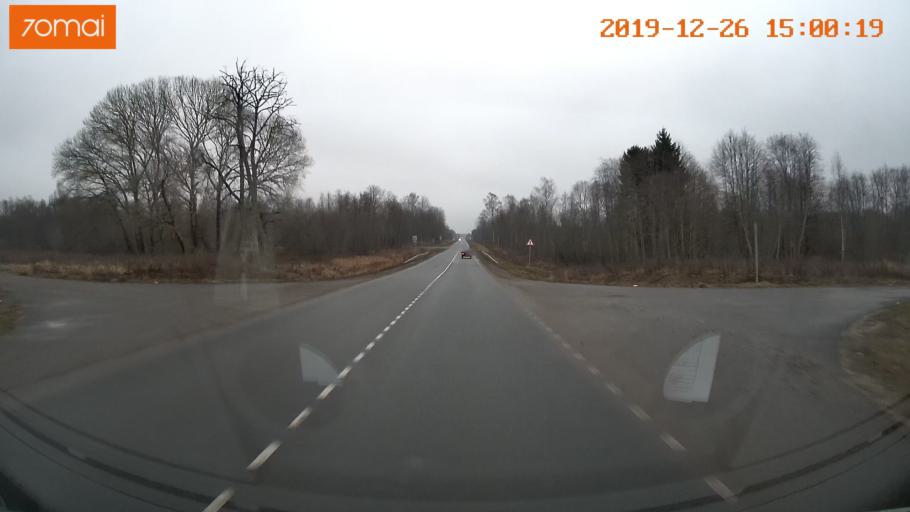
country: RU
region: Jaroslavl
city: Rybinsk
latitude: 58.2475
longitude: 38.8499
